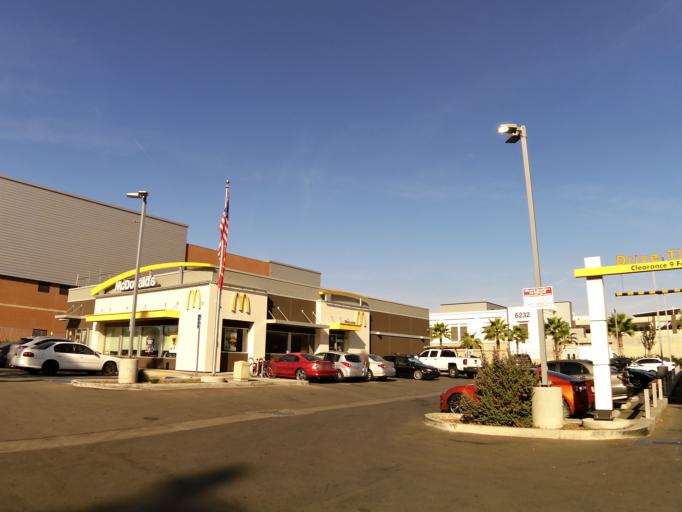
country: US
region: California
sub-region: Los Angeles County
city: Woodland Hills
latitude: 34.1831
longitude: -118.6041
